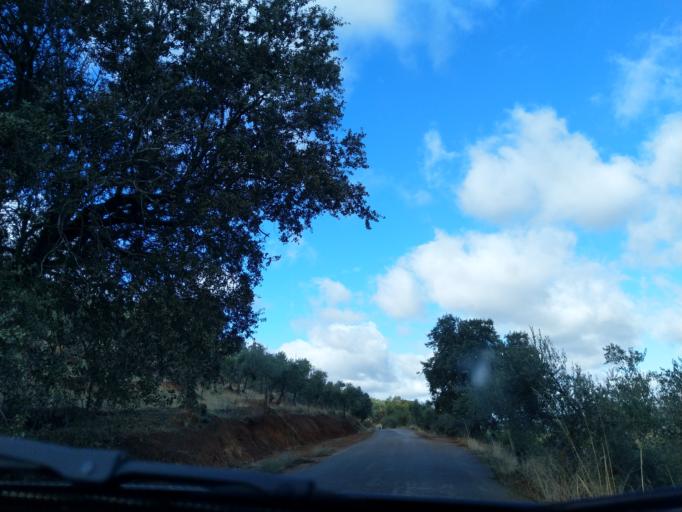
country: ES
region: Extremadura
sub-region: Provincia de Badajoz
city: Reina
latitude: 38.1266
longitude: -5.9193
